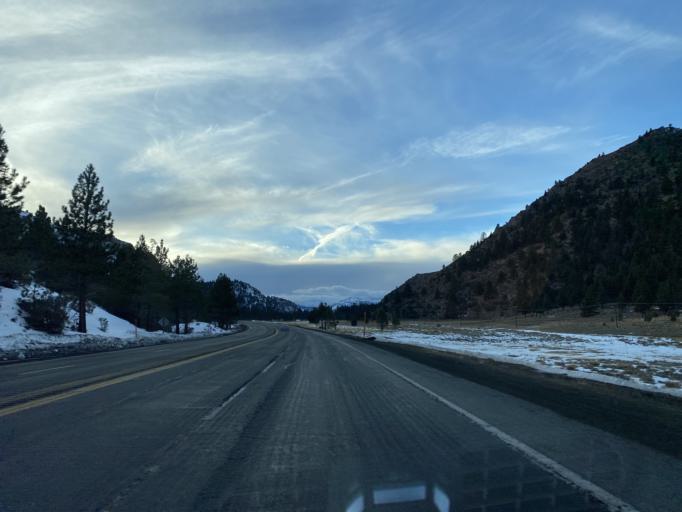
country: US
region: California
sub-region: Mono County
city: Bridgeport
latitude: 38.3490
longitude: -119.3452
